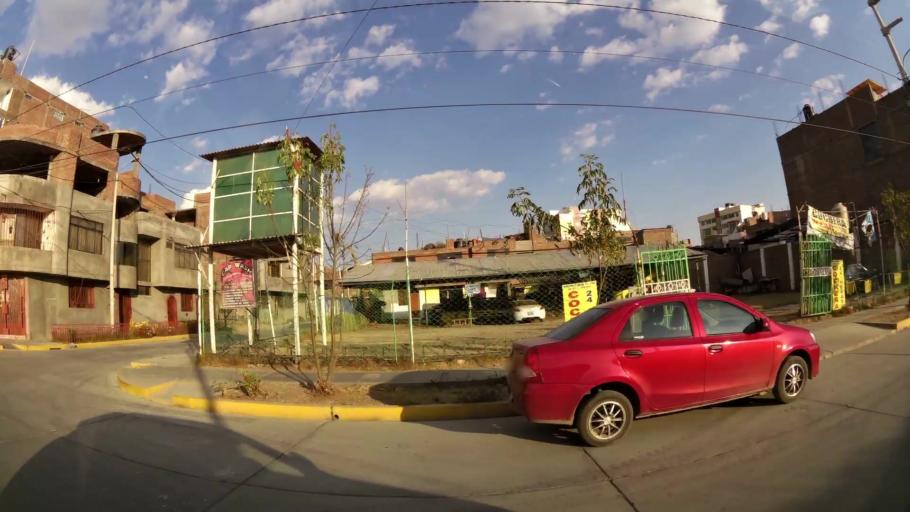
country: PE
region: Junin
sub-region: Provincia de Huancayo
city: El Tambo
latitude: -12.0497
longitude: -75.2238
